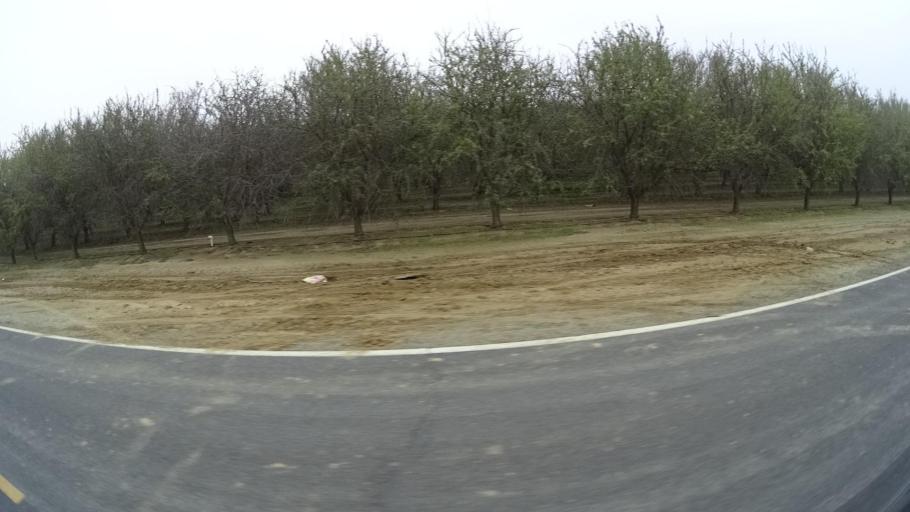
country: US
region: California
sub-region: Kern County
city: Lost Hills
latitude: 35.6147
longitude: -119.5803
